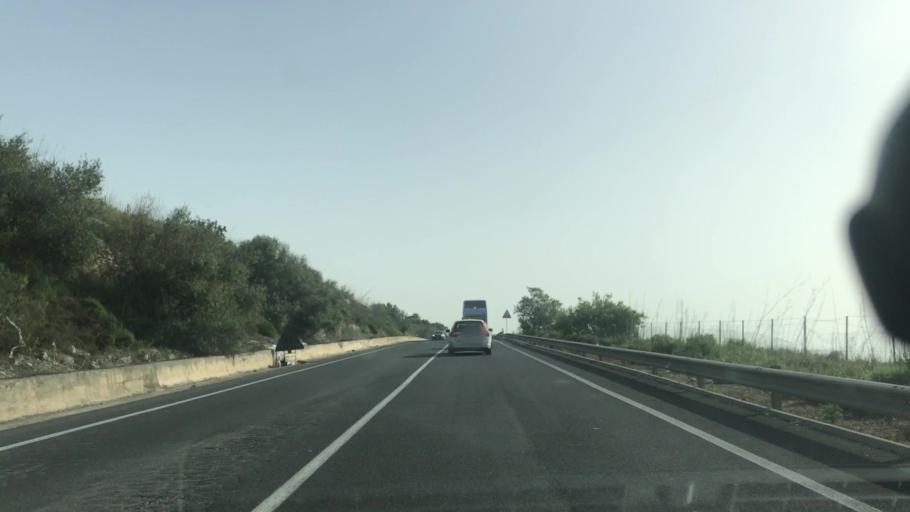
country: IT
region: Sicily
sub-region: Ragusa
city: Ragusa
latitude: 36.8704
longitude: 14.6860
